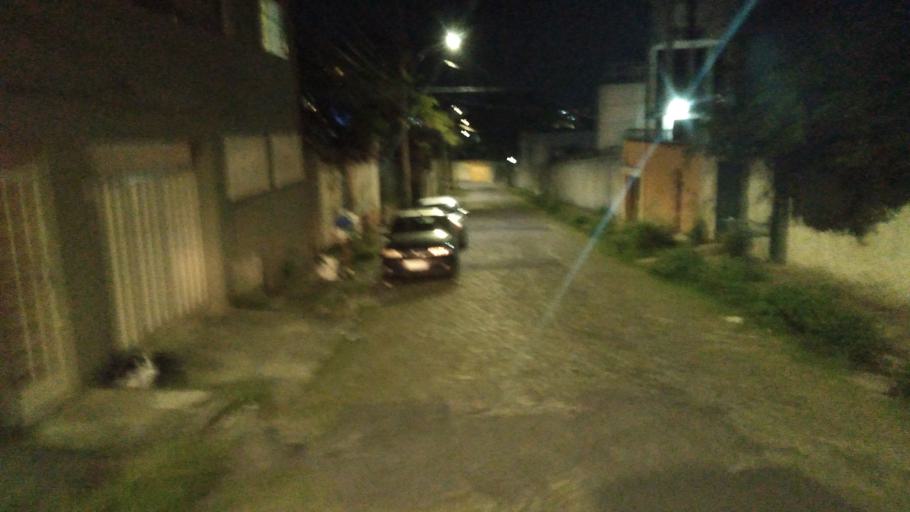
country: BR
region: Minas Gerais
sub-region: Belo Horizonte
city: Belo Horizonte
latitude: -19.9109
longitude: -43.9456
